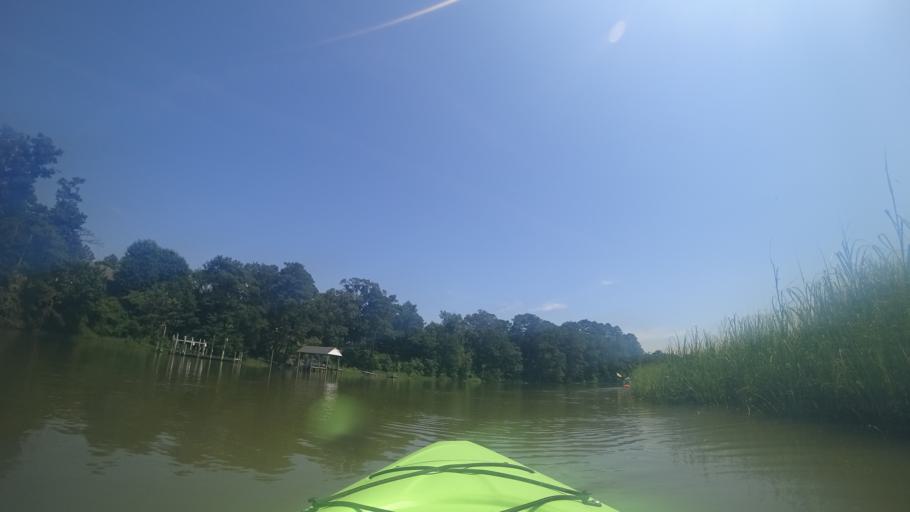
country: US
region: Virginia
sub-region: Isle of Wight County
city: Smithfield
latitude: 36.9680
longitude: -76.6125
